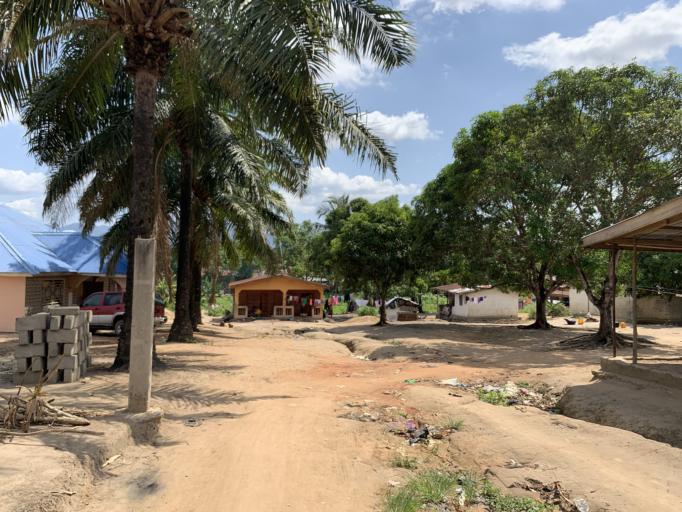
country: SL
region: Western Area
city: Waterloo
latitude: 8.3288
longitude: -13.0457
